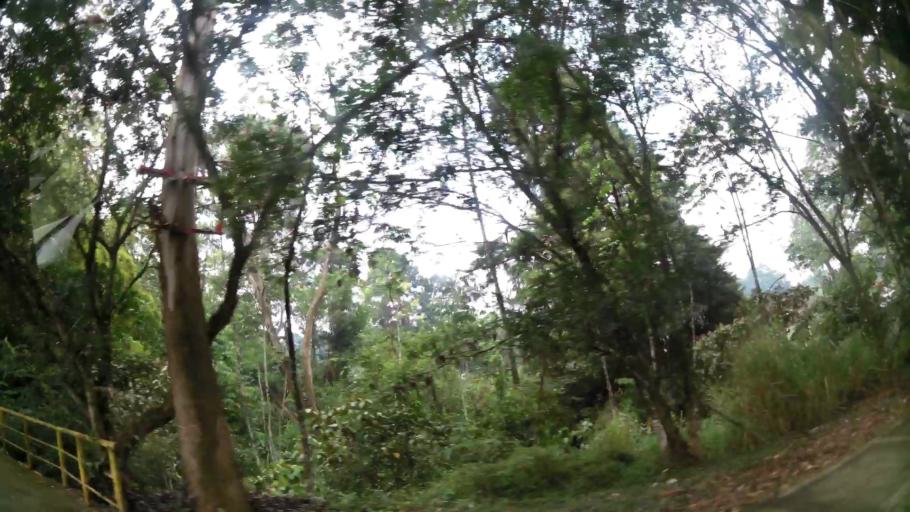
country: CO
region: Antioquia
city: Medellin
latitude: 6.2073
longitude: -75.5524
